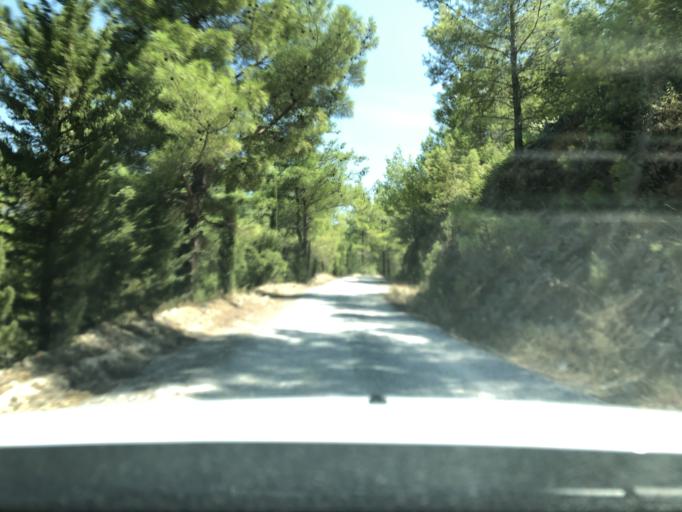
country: TR
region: Antalya
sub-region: Manavgat
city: Manavgat
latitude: 36.9059
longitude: 31.5589
